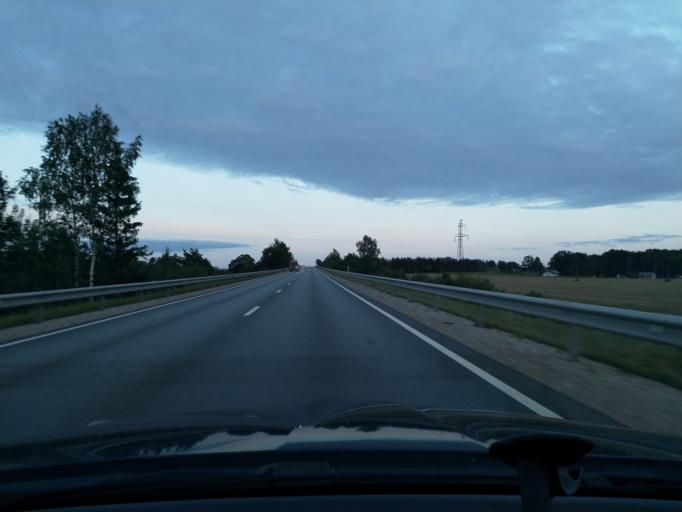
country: LV
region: Tukuma Rajons
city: Tukums
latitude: 56.9412
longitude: 23.1625
